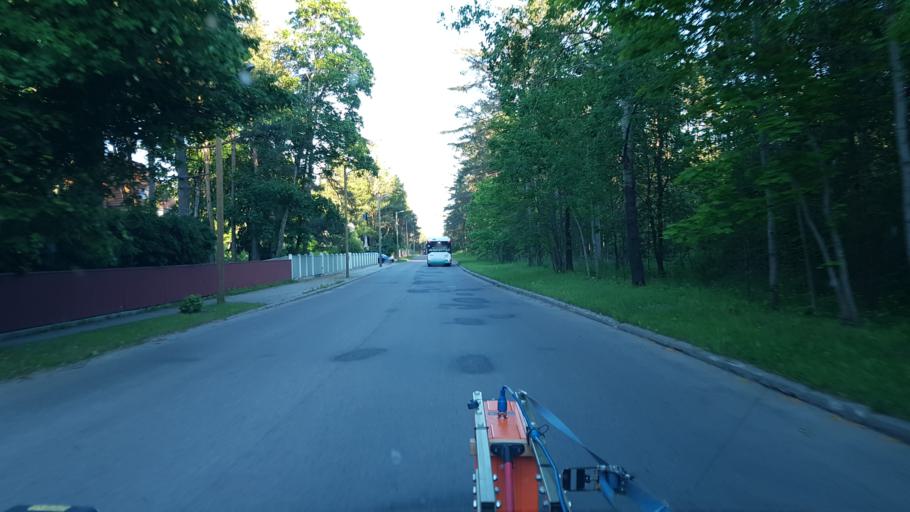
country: EE
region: Harju
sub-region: Saue vald
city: Laagri
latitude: 59.3775
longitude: 24.6705
